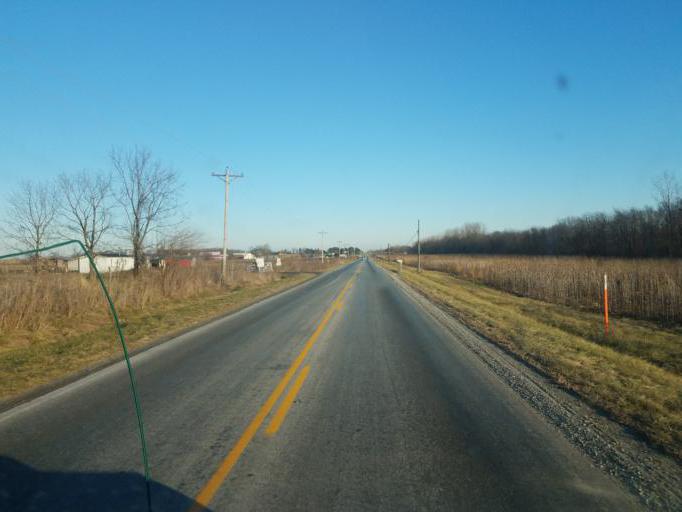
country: US
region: Ohio
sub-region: Hardin County
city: Kenton
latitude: 40.6243
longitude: -83.5294
